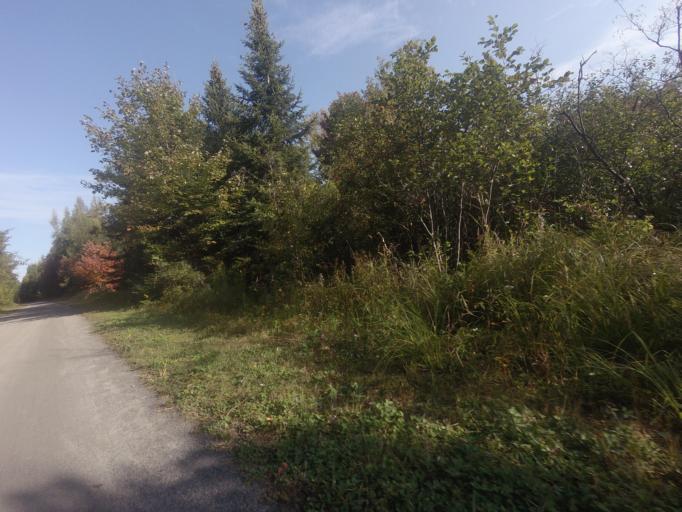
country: CA
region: Quebec
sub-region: Laurentides
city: Val-David
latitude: 46.0205
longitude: -74.1909
